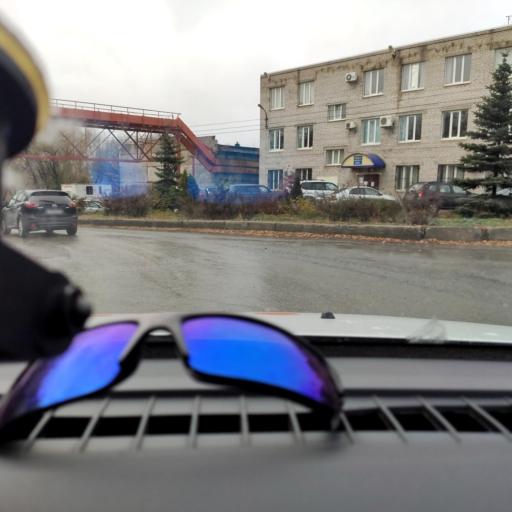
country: RU
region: Samara
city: Samara
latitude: 53.1858
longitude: 50.1594
